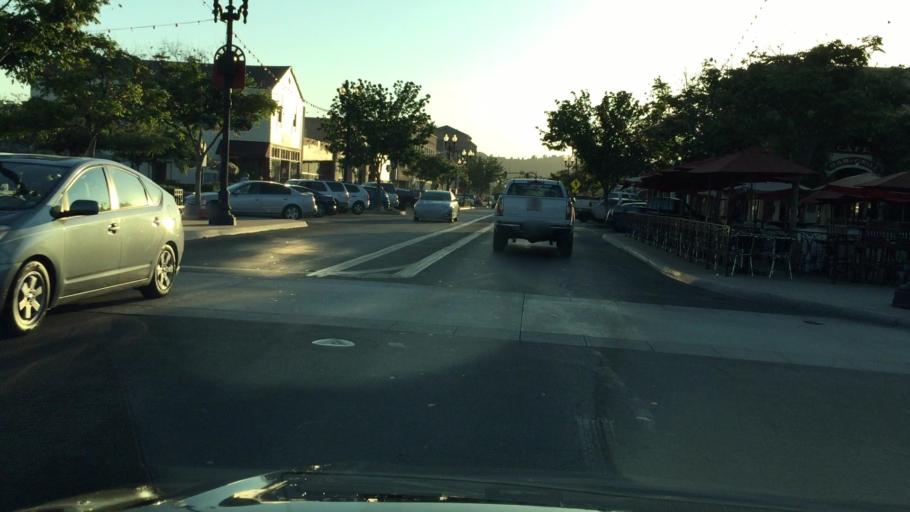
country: US
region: California
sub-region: San Diego County
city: El Cajon
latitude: 32.7950
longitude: -116.9602
